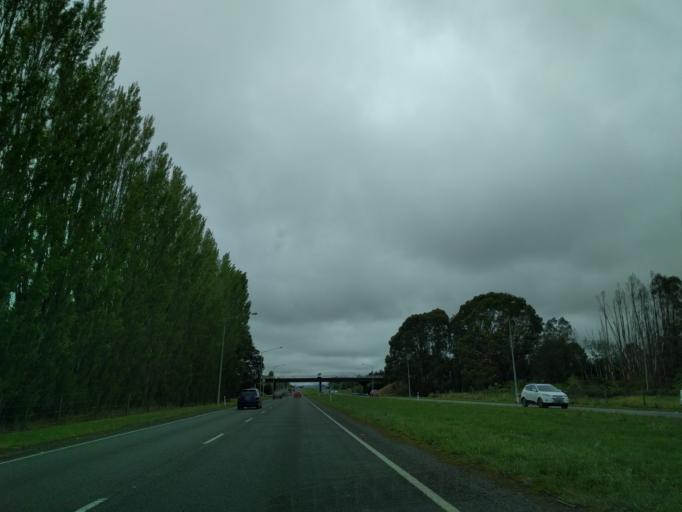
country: NZ
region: Canterbury
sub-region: Waimakariri District
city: Kaiapoi
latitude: -43.4059
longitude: 172.6441
